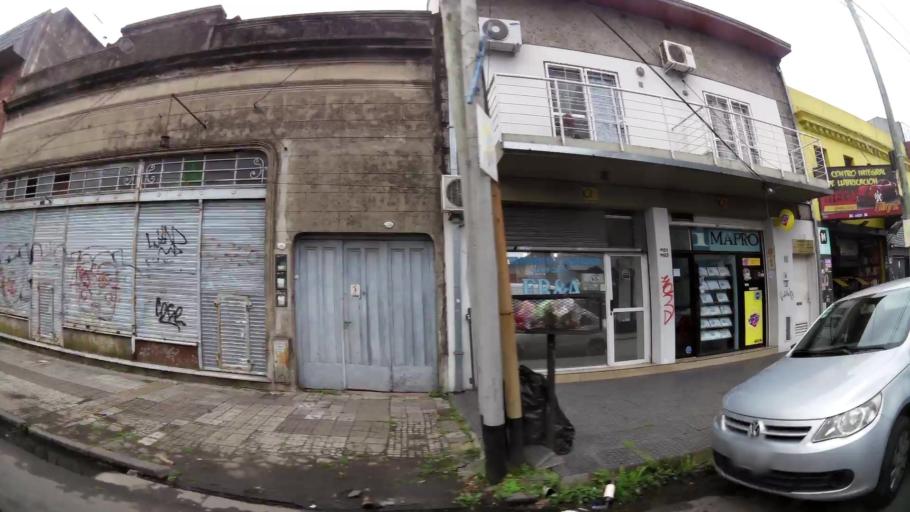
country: AR
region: Buenos Aires
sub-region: Partido de Lanus
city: Lanus
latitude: -34.7008
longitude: -58.3824
